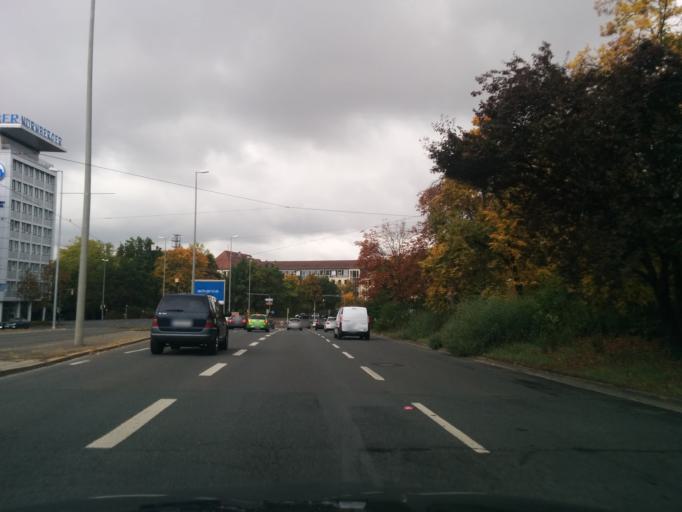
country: DE
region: Bavaria
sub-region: Regierungsbezirk Mittelfranken
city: Nuernberg
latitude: 49.4569
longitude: 11.0891
